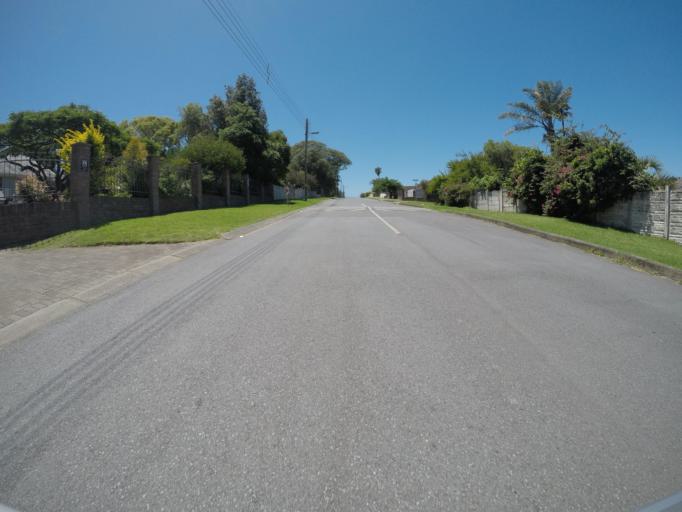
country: ZA
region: Eastern Cape
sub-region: Buffalo City Metropolitan Municipality
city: East London
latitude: -32.9631
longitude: 27.9359
